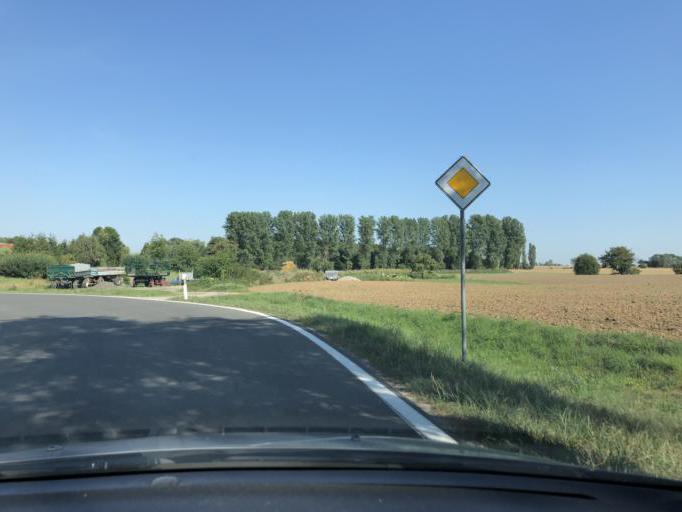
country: DE
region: Thuringia
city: Rastenberg
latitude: 51.1954
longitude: 11.4724
